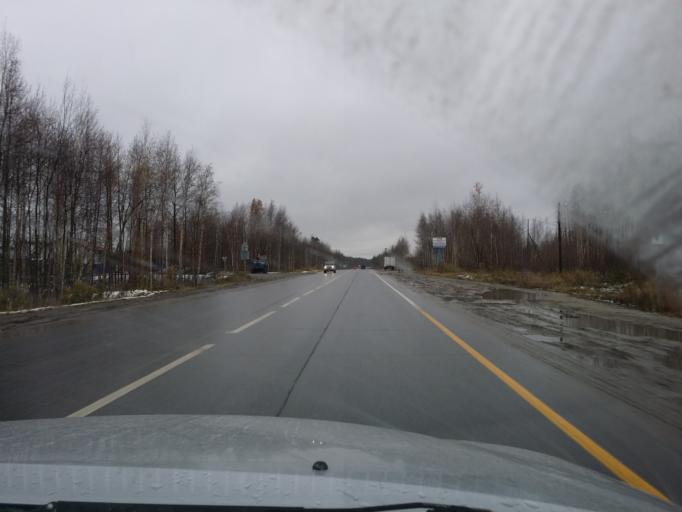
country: RU
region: Khanty-Mansiyskiy Avtonomnyy Okrug
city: Megion
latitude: 61.0904
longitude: 76.0935
